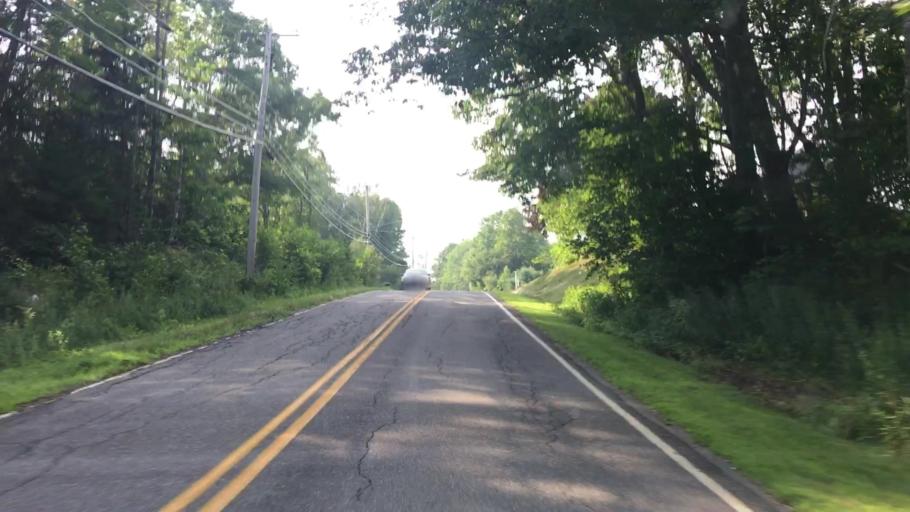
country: US
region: Maine
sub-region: Lincoln County
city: Waldoboro
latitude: 44.0540
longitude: -69.3362
